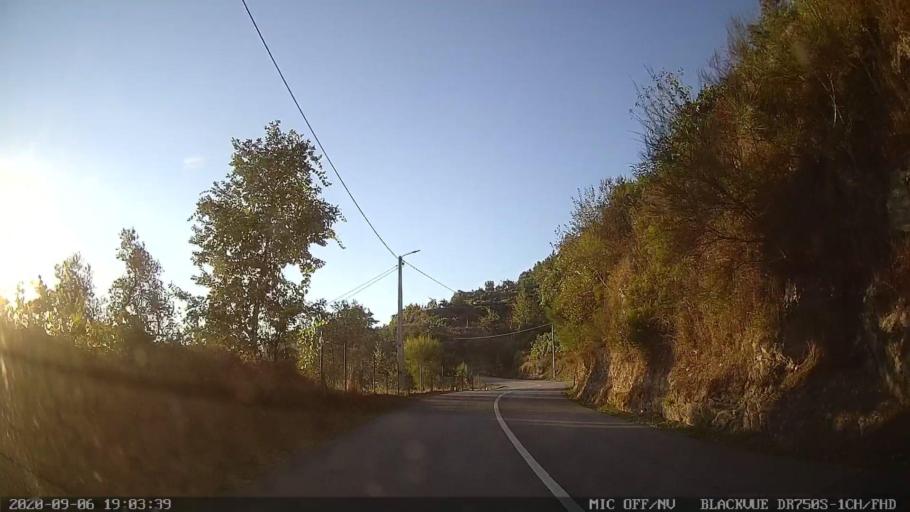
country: PT
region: Porto
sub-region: Baiao
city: Baiao
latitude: 41.2311
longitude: -7.9957
